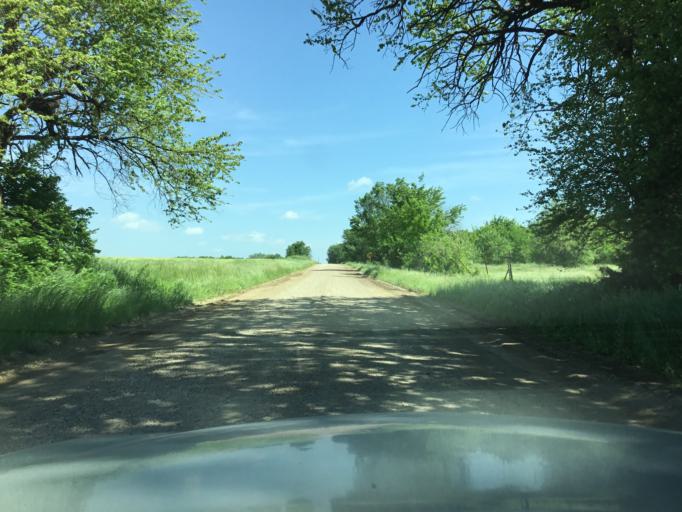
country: US
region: Kansas
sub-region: Labette County
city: Oswego
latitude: 37.1861
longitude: -95.1400
